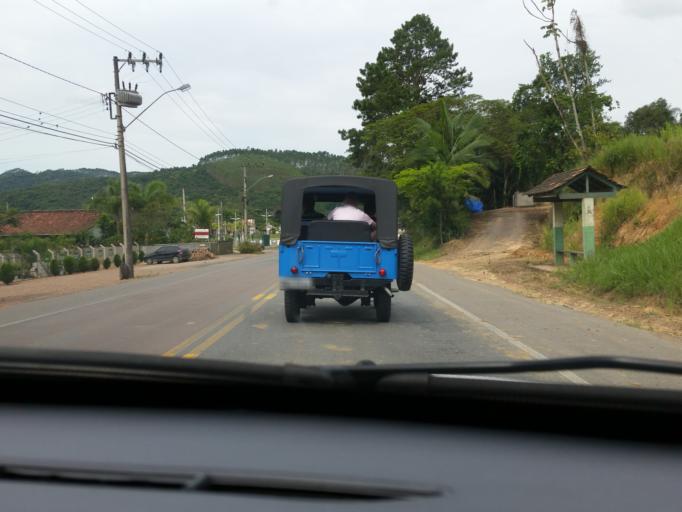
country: BR
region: Santa Catarina
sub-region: Rodeio
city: Gavea
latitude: -27.0269
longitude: -49.3787
